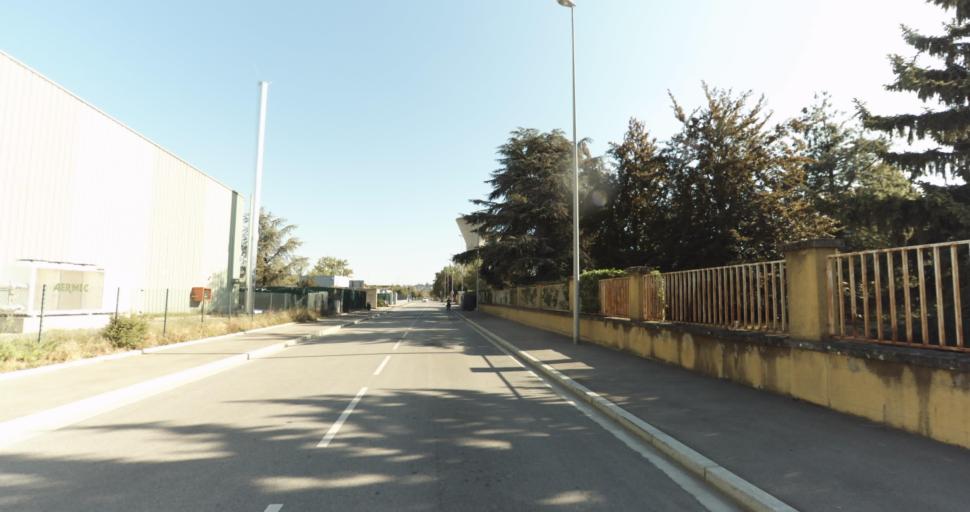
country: FR
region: Rhone-Alpes
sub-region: Departement du Rhone
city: Genay
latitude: 45.8845
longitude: 4.8177
